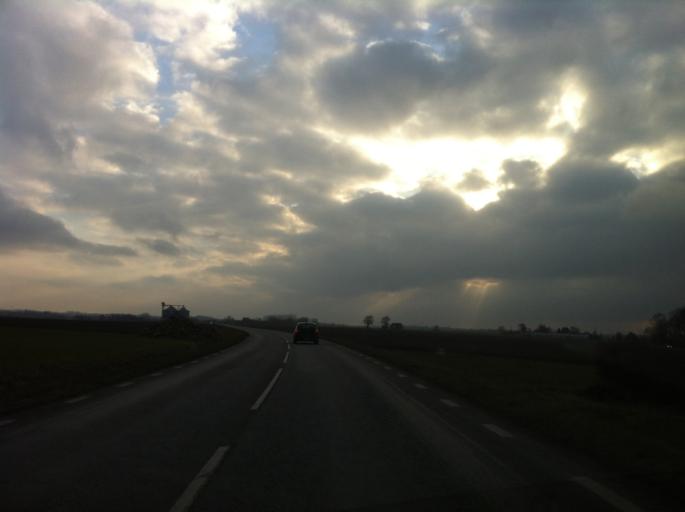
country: SE
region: Skane
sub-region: Kavlinge Kommun
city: Kaevlinge
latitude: 55.7801
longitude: 13.0661
